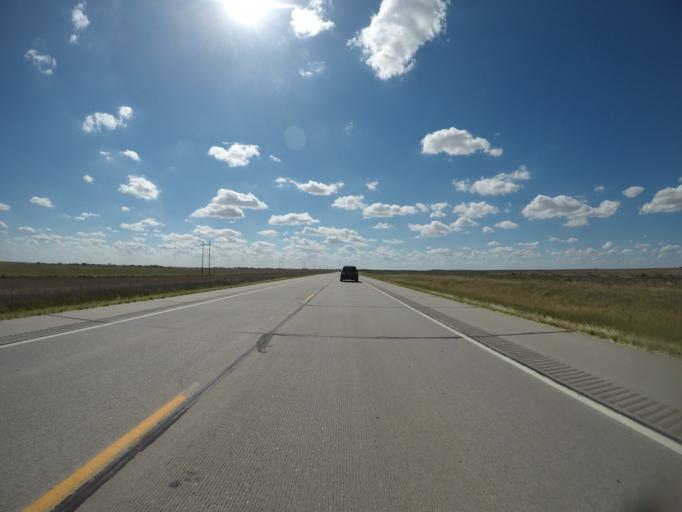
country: US
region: Colorado
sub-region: Phillips County
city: Holyoke
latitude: 40.5944
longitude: -102.3644
